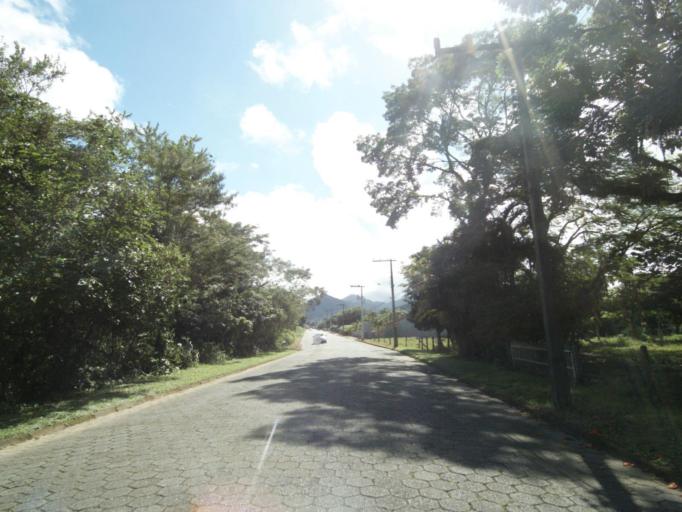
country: BR
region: Santa Catarina
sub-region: Pomerode
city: Pomerode
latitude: -26.6973
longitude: -49.1733
